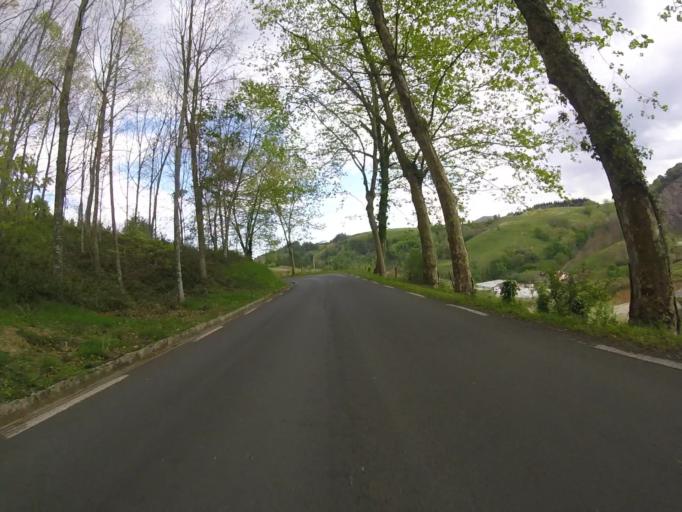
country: ES
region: Basque Country
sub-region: Provincia de Guipuzcoa
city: Zarautz
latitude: 43.2681
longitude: -2.1674
